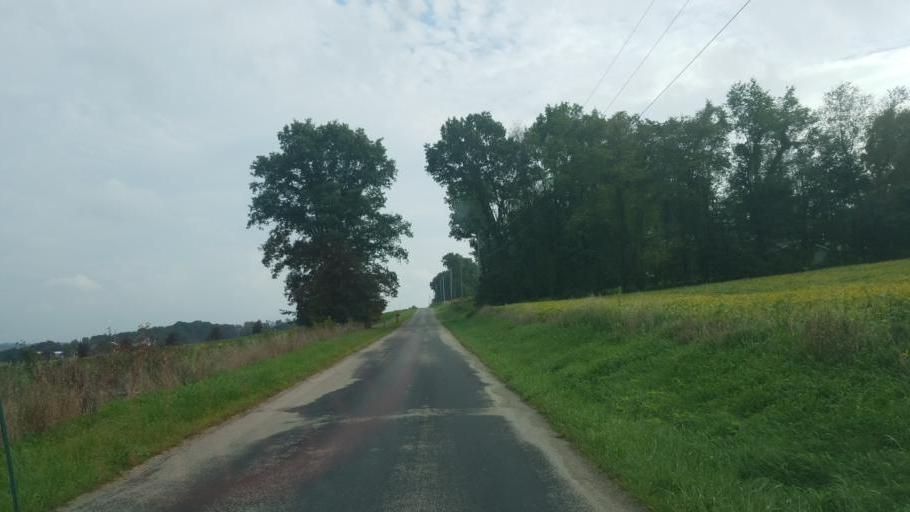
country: US
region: Ohio
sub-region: Wayne County
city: West Salem
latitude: 40.8952
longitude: -82.0235
